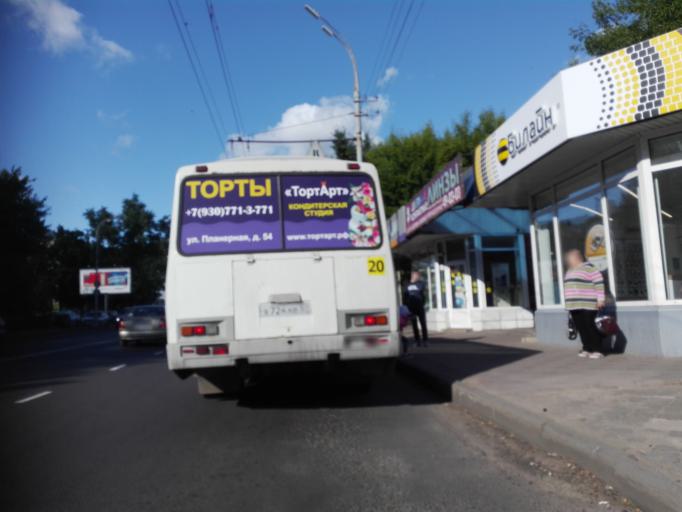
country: RU
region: Orjol
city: Orel
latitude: 52.9794
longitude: 36.1051
